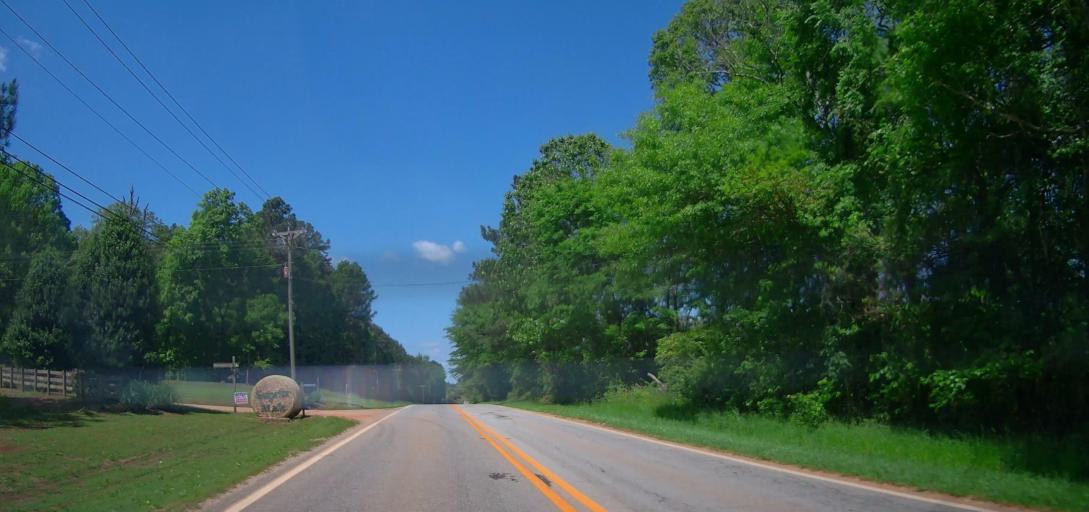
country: US
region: Georgia
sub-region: Putnam County
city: Eatonton
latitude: 33.3147
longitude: -83.2996
